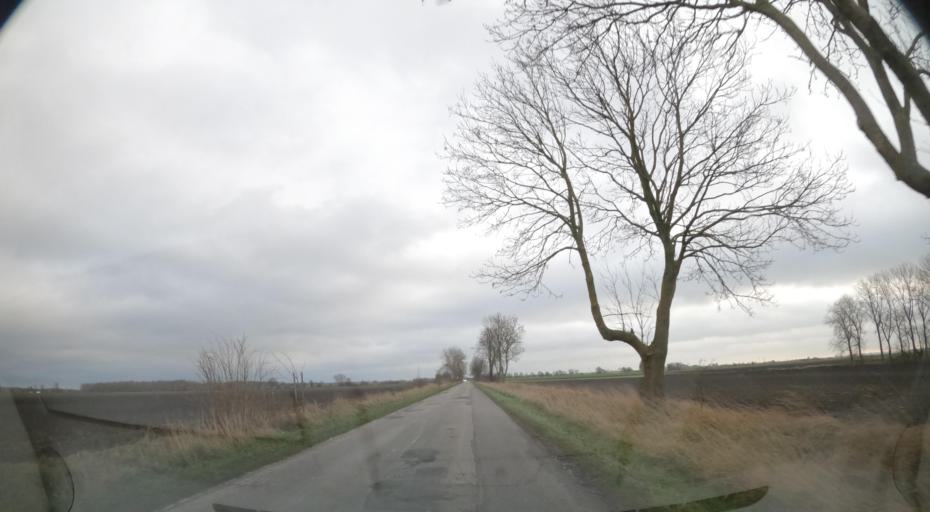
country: PL
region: Greater Poland Voivodeship
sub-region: Powiat pilski
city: Lobzenica
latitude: 53.2667
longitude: 17.2089
